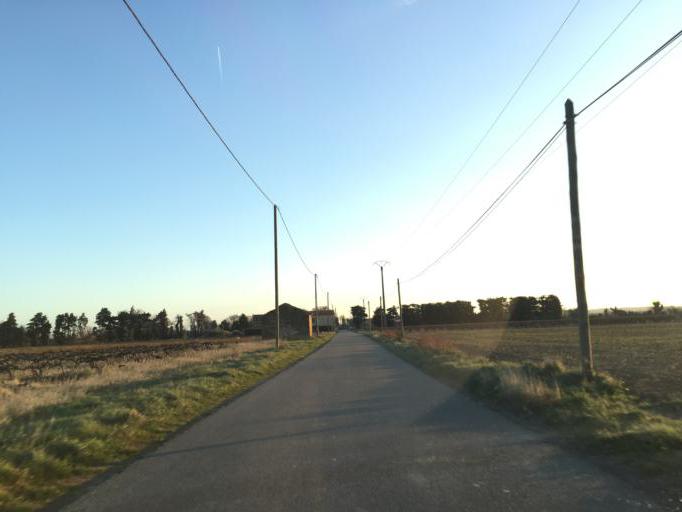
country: FR
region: Provence-Alpes-Cote d'Azur
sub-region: Departement du Vaucluse
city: Camaret-sur-Aigues
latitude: 44.1459
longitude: 4.8752
